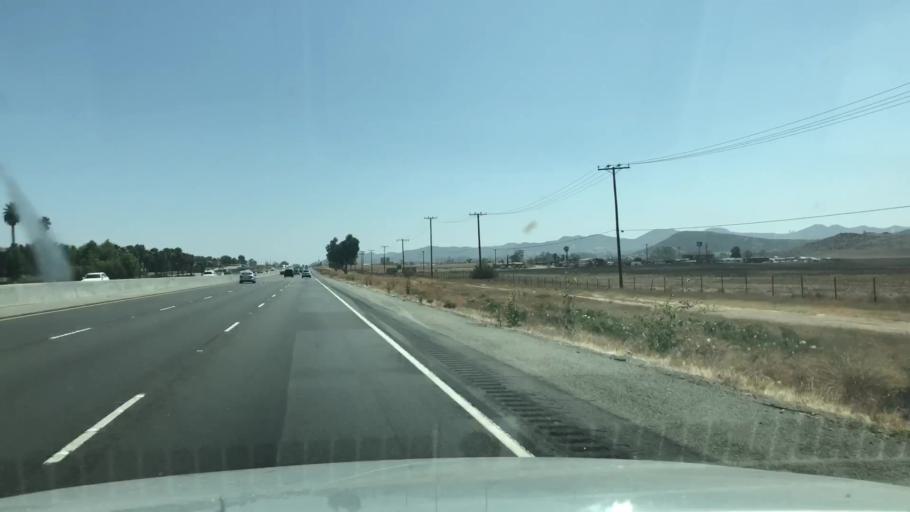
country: US
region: California
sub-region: Riverside County
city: Sun City
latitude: 33.6744
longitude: -117.1711
